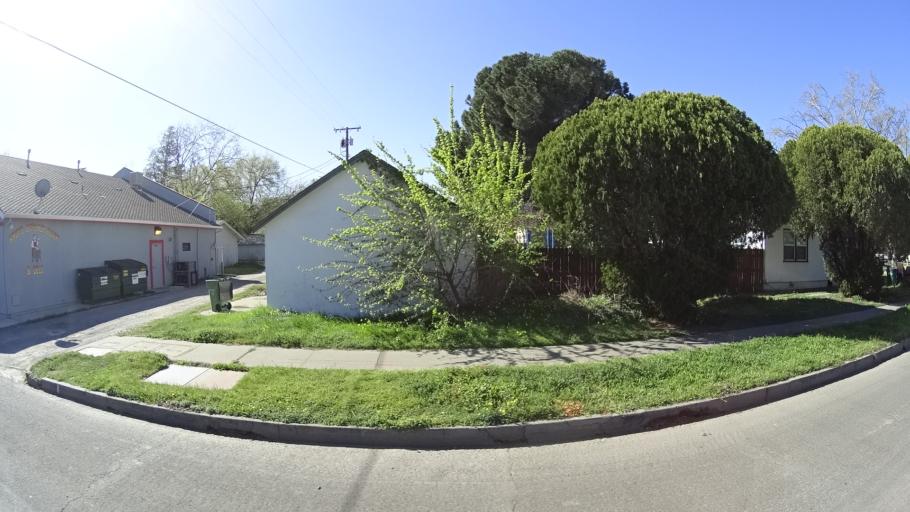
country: US
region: California
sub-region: Glenn County
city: Orland
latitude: 39.7473
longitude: -122.1910
